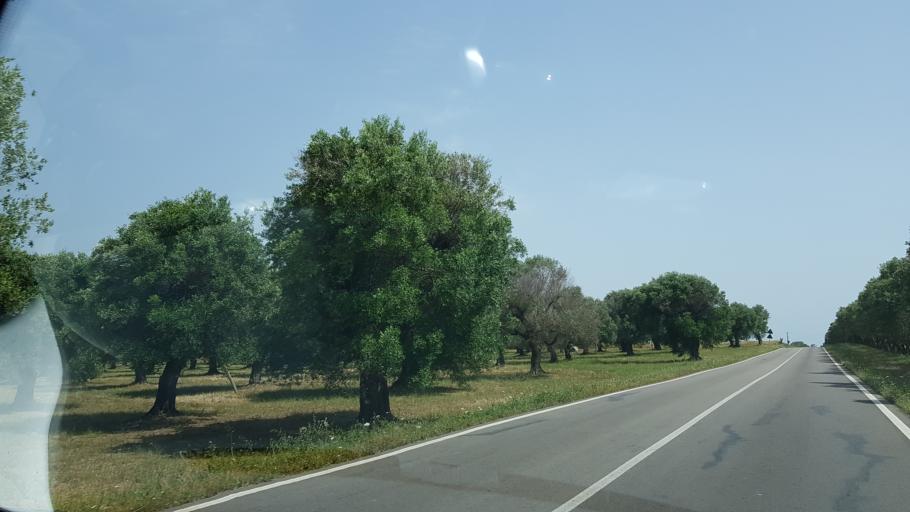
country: IT
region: Apulia
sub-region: Provincia di Brindisi
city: San Pancrazio Salentino
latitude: 40.3703
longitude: 17.8396
